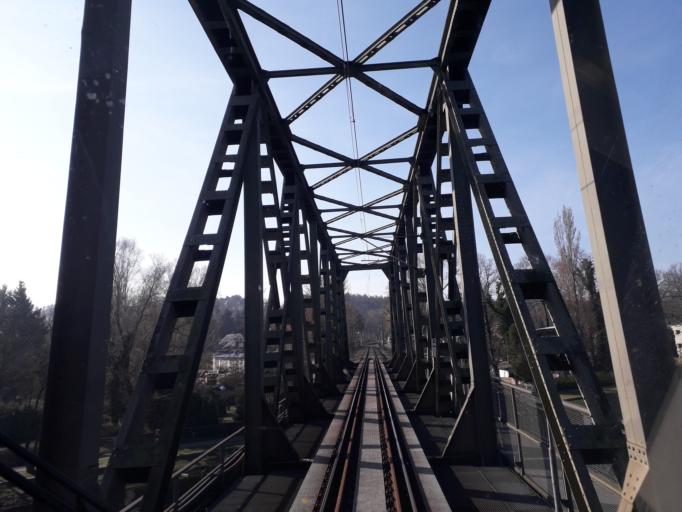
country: DE
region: Brandenburg
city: Michendorf
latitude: 52.3434
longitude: 12.9806
